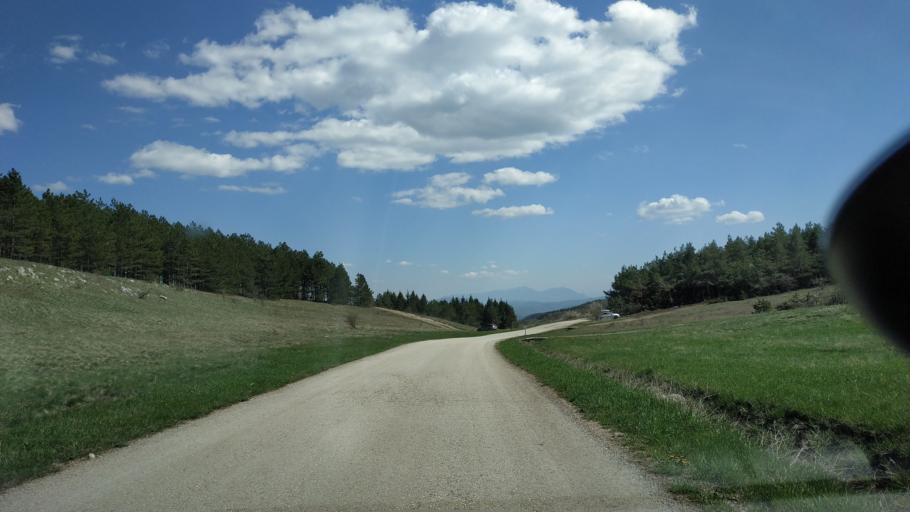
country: RS
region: Central Serbia
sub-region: Zajecarski Okrug
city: Soko Banja
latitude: 43.5915
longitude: 21.8874
